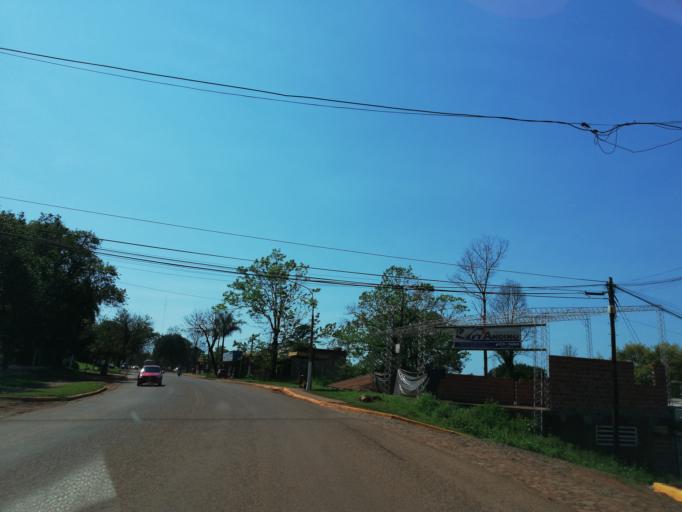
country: AR
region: Misiones
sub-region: Departamento de Eldorado
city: Eldorado
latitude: -26.4092
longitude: -54.6456
